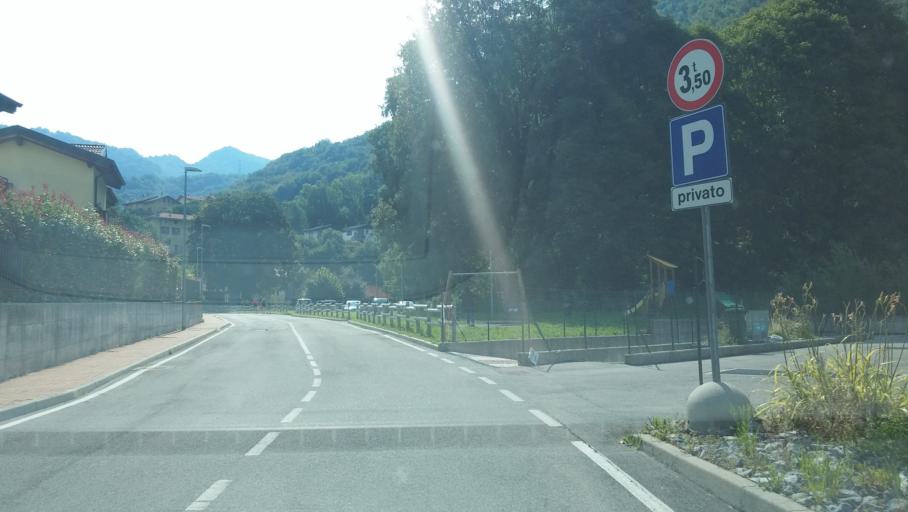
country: IT
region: Lombardy
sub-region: Provincia di Lecco
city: Cremeno
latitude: 45.9220
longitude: 9.4499
